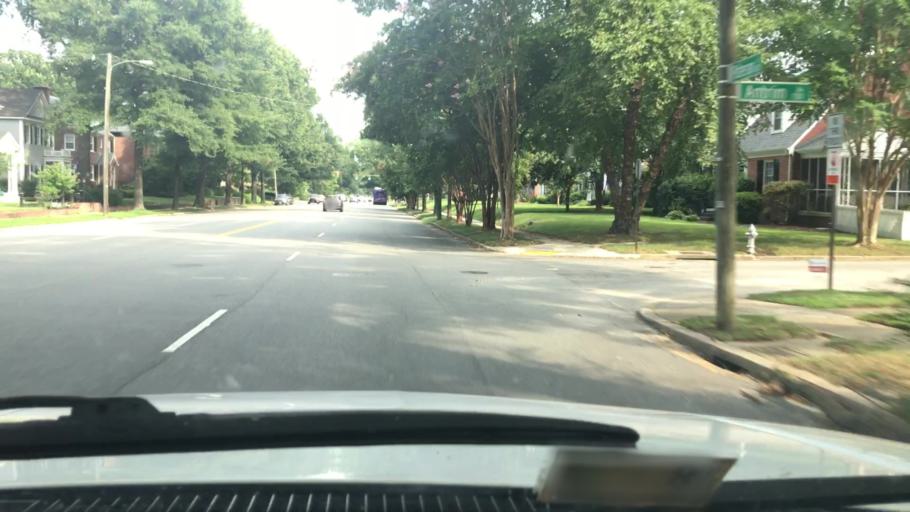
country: US
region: Virginia
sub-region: City of Richmond
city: Richmond
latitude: 37.5669
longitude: -77.4911
